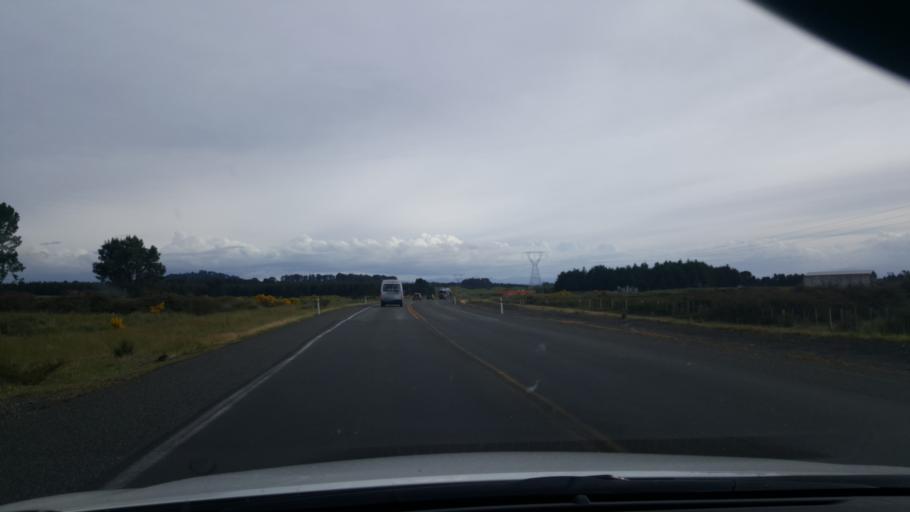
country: NZ
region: Waikato
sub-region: Taupo District
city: Taupo
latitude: -38.6930
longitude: 176.1138
